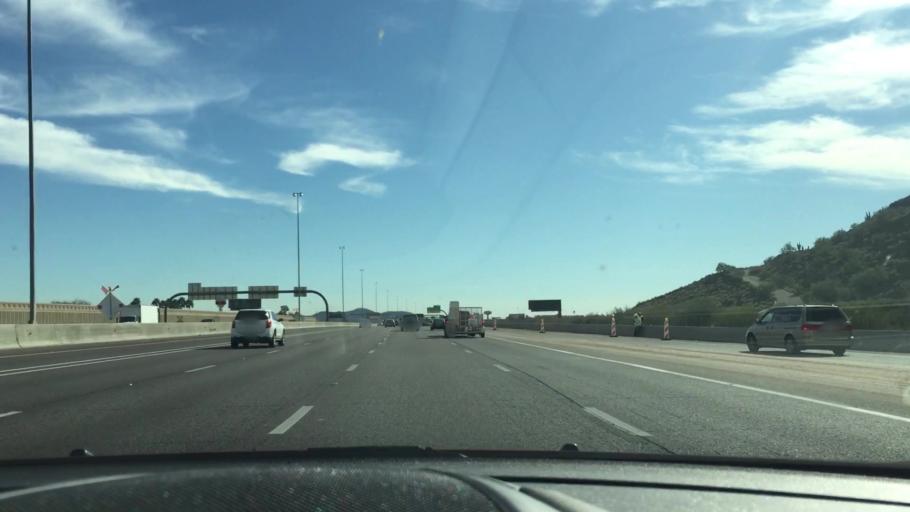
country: US
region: Arizona
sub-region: Maricopa County
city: Peoria
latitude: 33.6966
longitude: -112.1159
